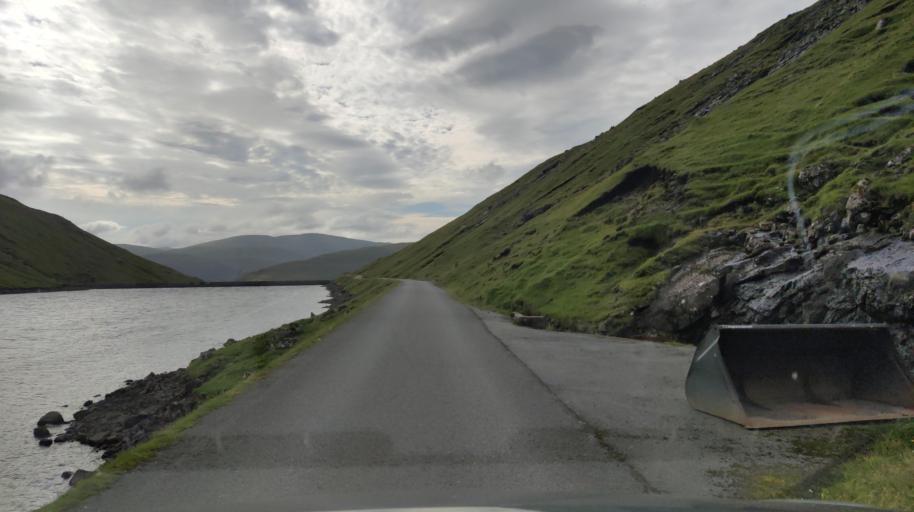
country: FO
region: Streymoy
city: Vestmanna
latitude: 62.1547
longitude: -7.1209
